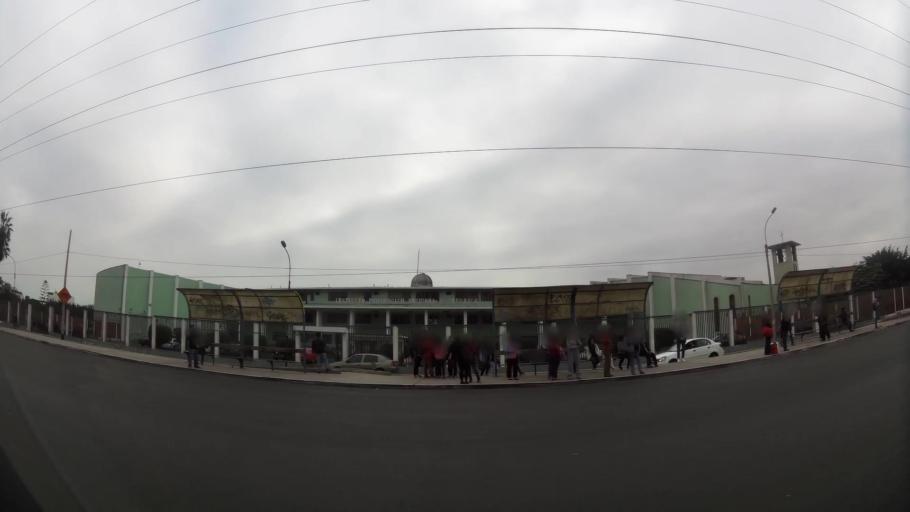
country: PE
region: Lima
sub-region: Lima
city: Surco
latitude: -12.1227
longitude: -76.9772
